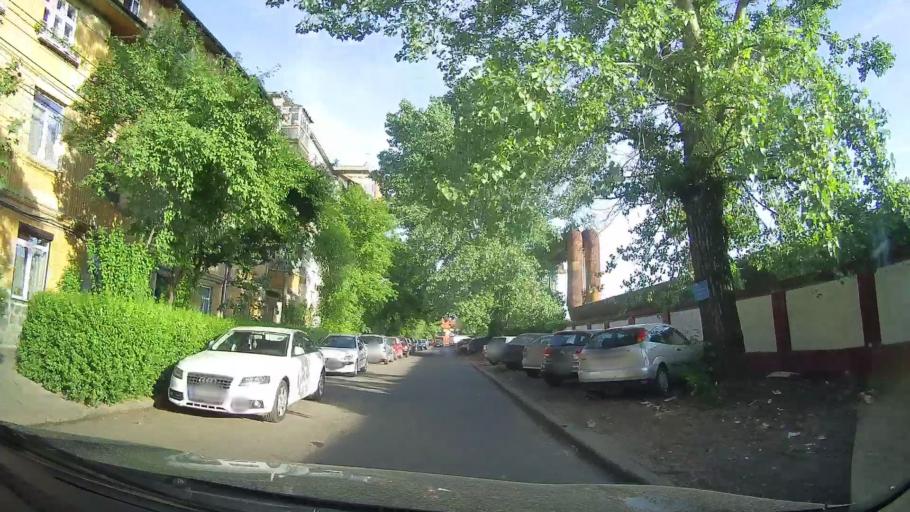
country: RO
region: Timis
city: Timisoara
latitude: 45.7481
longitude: 21.2457
